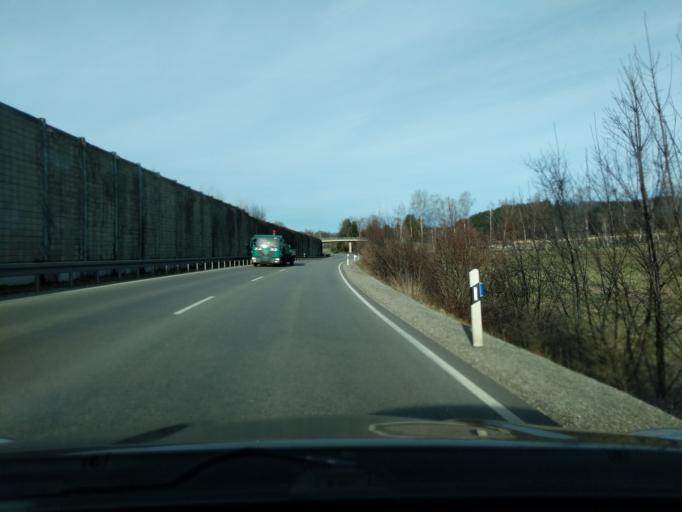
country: DE
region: Bavaria
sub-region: Upper Bavaria
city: Ebersberg
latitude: 48.0716
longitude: 11.9784
